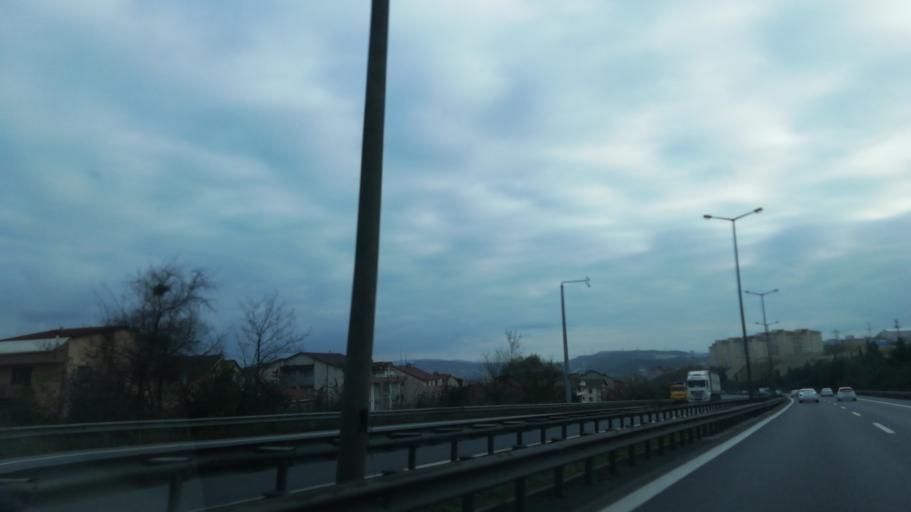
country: TR
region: Kocaeli
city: Izmit
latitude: 40.7855
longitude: 29.9562
